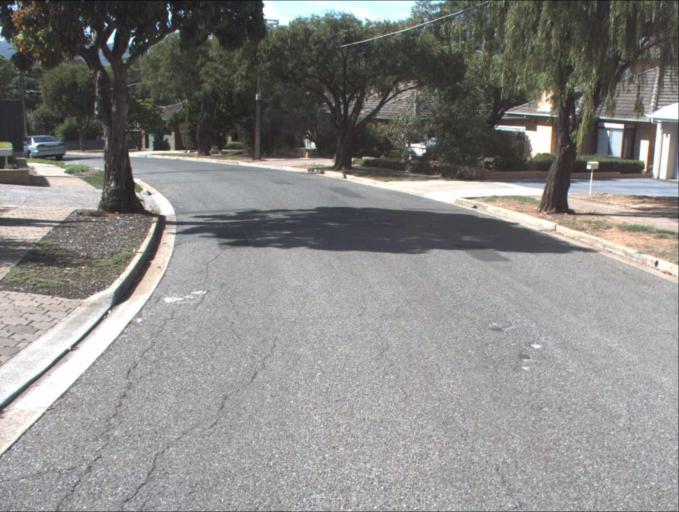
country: AU
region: South Australia
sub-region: Port Adelaide Enfield
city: Gilles Plains
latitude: -34.8638
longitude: 138.6545
